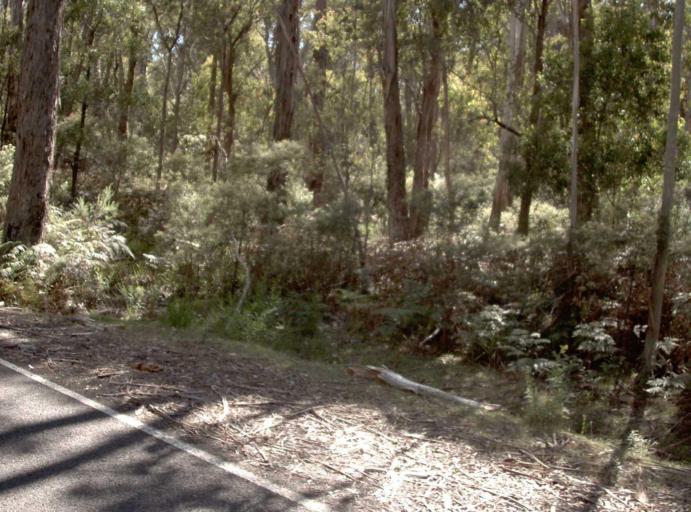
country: AU
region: New South Wales
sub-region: Bombala
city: Bombala
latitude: -37.1358
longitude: 148.7401
